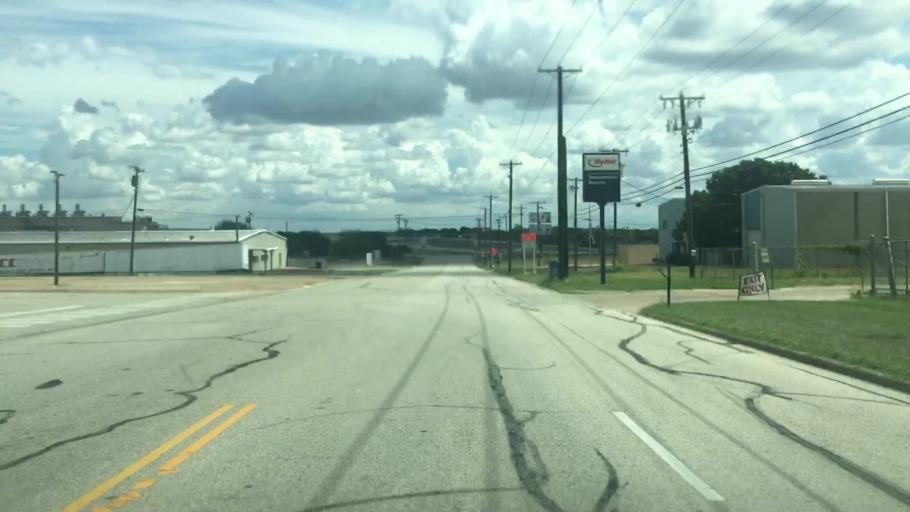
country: US
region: Texas
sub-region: Bell County
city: Temple
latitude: 31.1274
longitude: -97.3450
